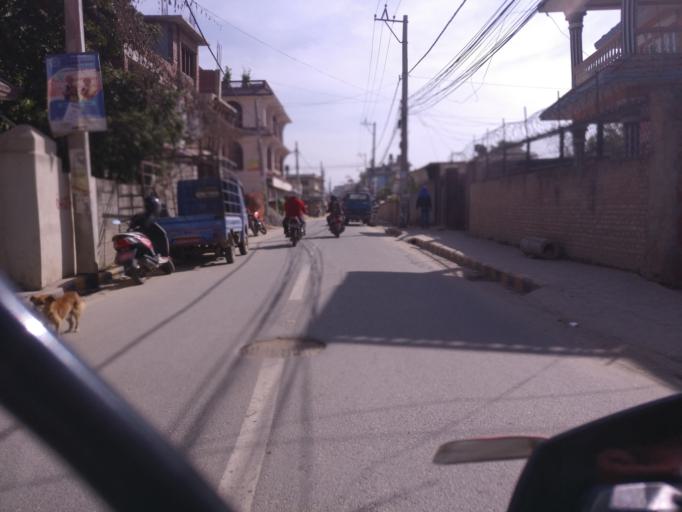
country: NP
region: Central Region
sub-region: Bagmati Zone
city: Patan
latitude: 27.6617
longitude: 85.3156
